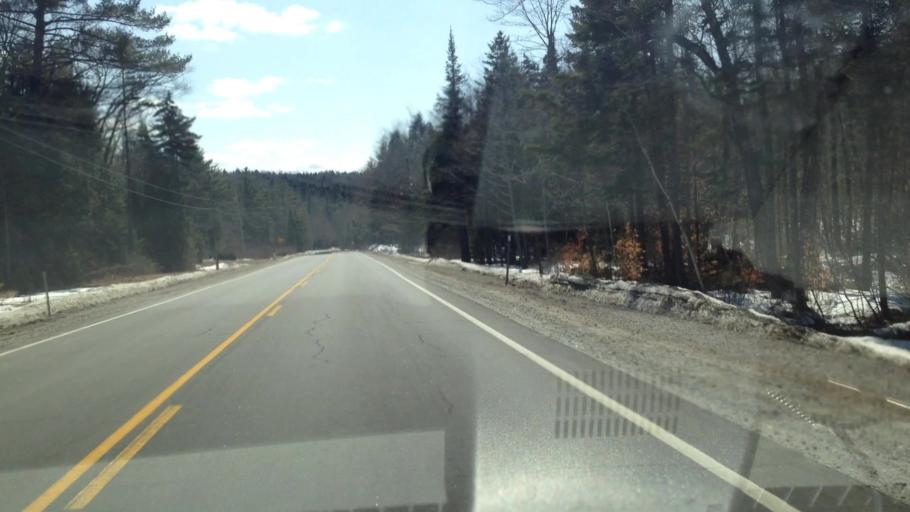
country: US
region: New Hampshire
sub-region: Merrimack County
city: Wilmot
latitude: 43.4685
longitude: -71.9606
